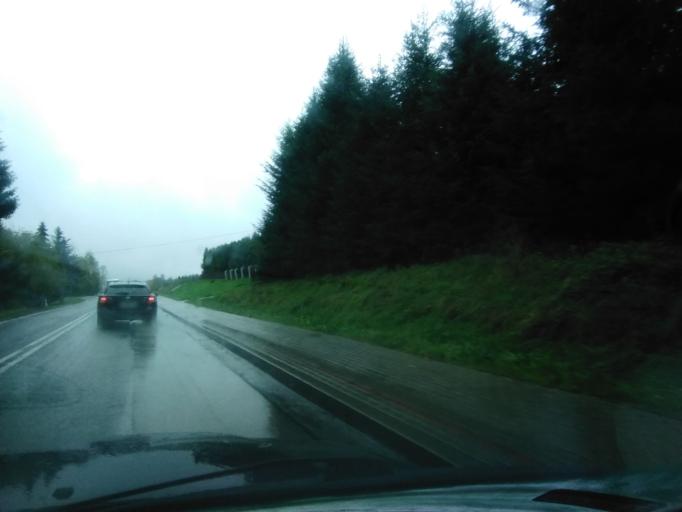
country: PL
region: Subcarpathian Voivodeship
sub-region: Powiat ropczycko-sedziszowski
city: Niedzwiada
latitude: 49.9996
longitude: 21.5613
